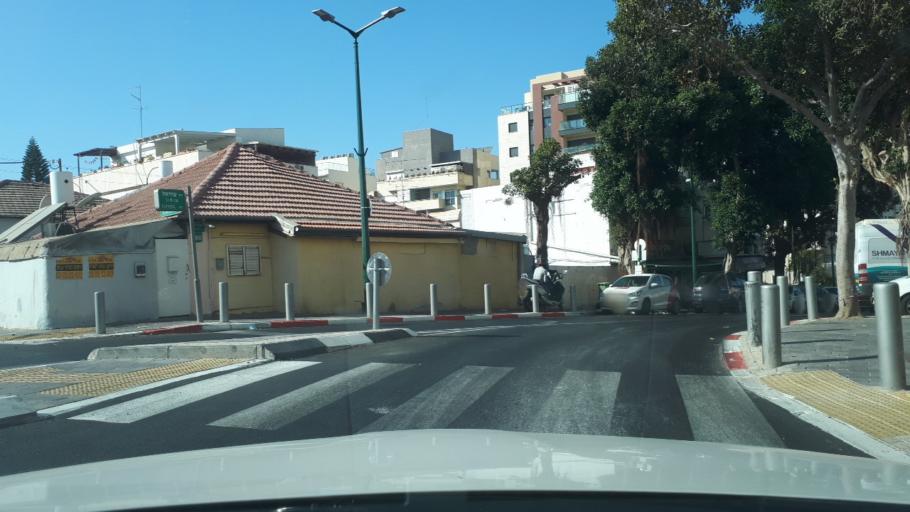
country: IL
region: Tel Aviv
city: Giv`atayim
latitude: 32.0706
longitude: 34.8227
